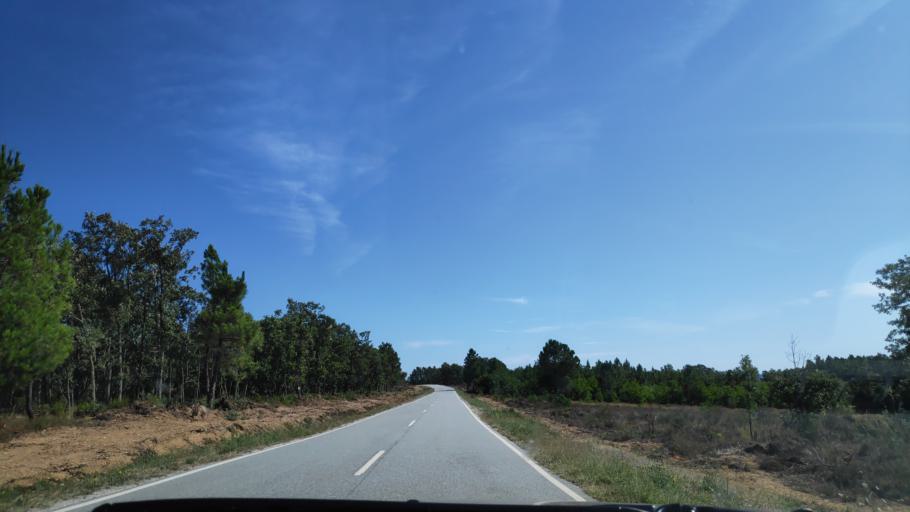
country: PT
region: Braganca
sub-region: Miranda do Douro
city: Miranda do Douro
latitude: 41.5767
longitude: -6.3589
